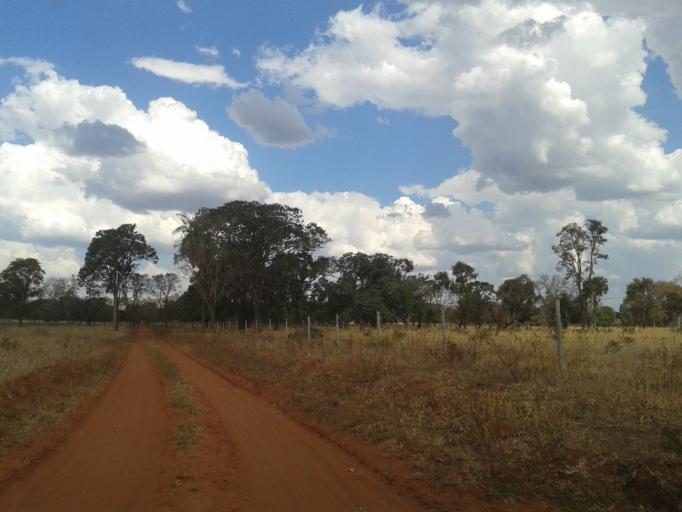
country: BR
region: Minas Gerais
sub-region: Santa Vitoria
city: Santa Vitoria
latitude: -19.1903
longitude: -49.9779
